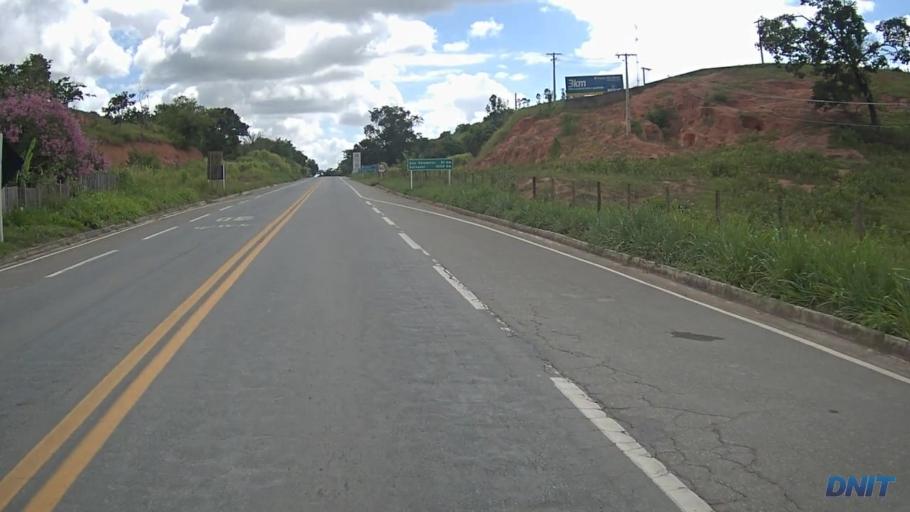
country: BR
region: Minas Gerais
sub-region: Governador Valadares
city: Governador Valadares
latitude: -18.9550
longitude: -42.0749
